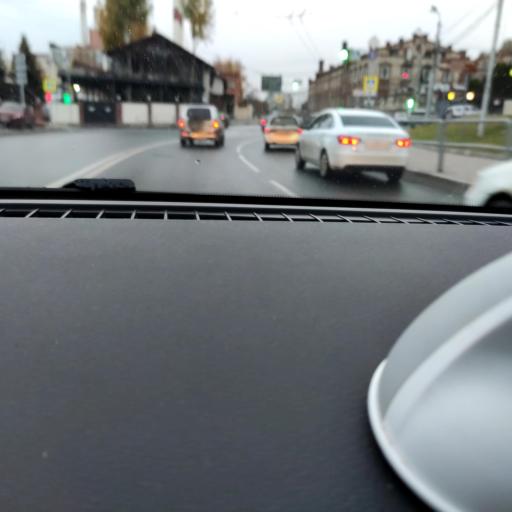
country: RU
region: Samara
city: Samara
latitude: 53.2008
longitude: 50.0993
